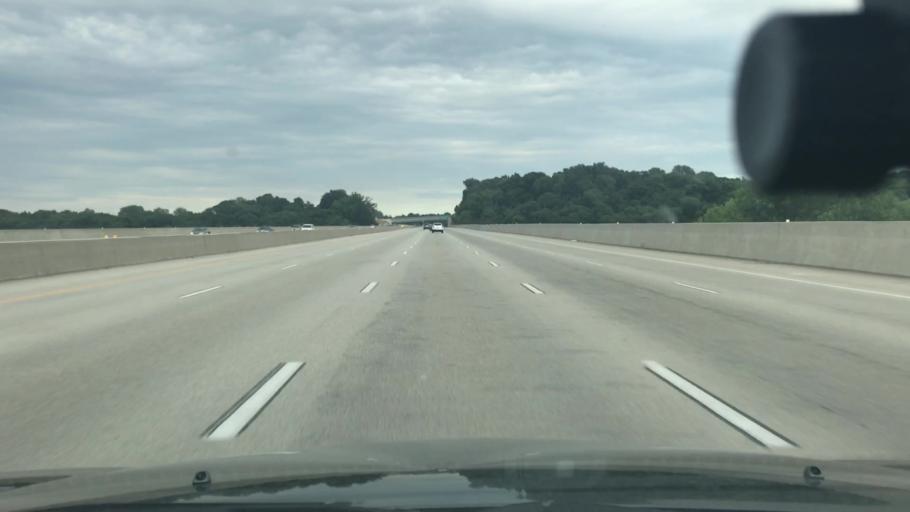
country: US
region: Missouri
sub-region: Saint Louis County
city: Maryland Heights
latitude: 38.7062
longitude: -90.4892
